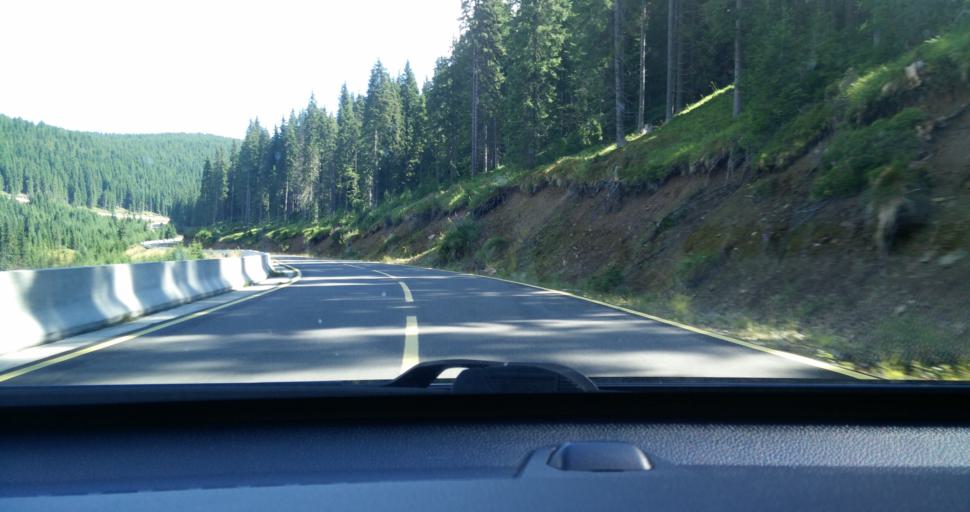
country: RO
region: Hunedoara
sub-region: Oras Petrila
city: Petrila
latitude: 45.4578
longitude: 23.6148
